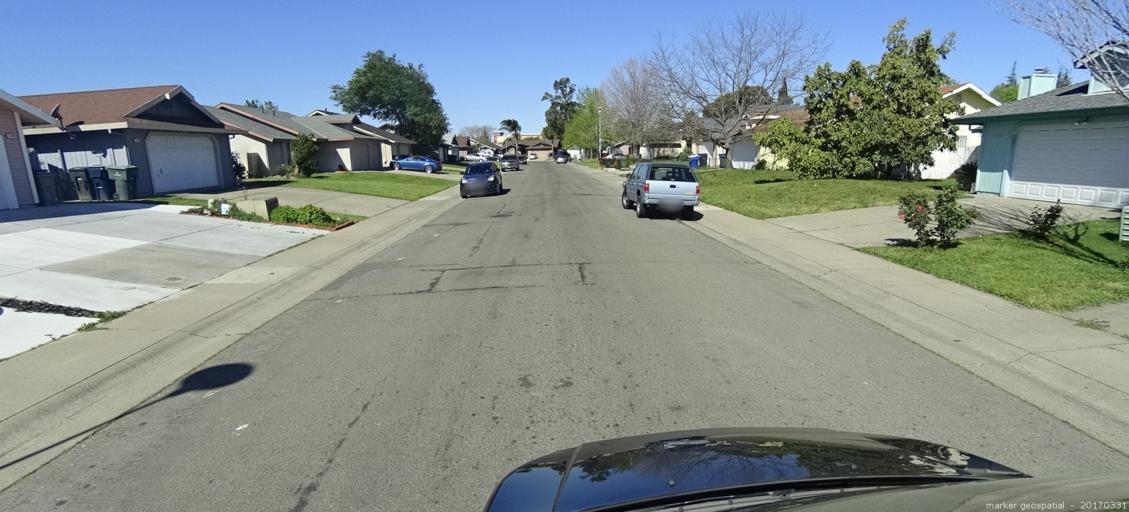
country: US
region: California
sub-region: Sacramento County
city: Parkway
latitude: 38.4728
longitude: -121.4429
